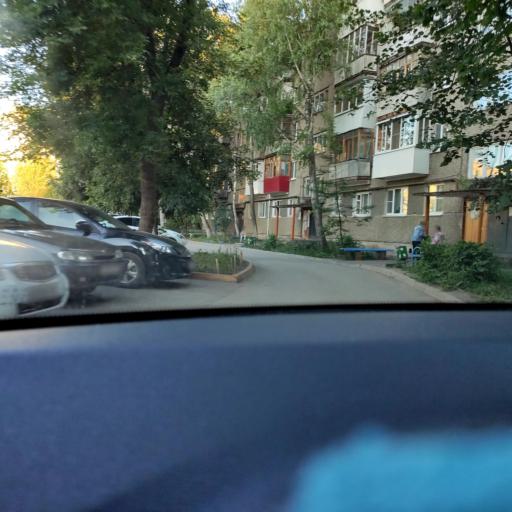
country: RU
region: Samara
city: Smyshlyayevka
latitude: 53.2524
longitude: 50.3763
